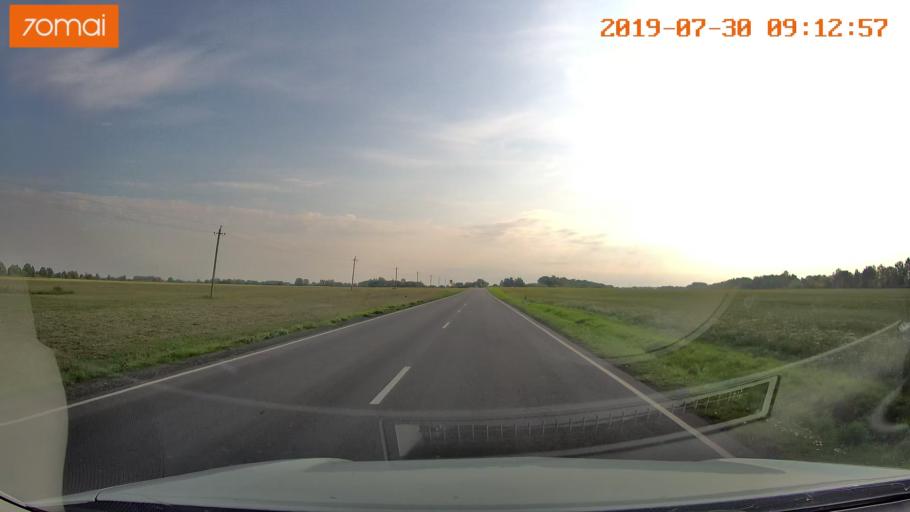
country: RU
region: Kaliningrad
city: Nesterov
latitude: 54.6209
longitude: 22.4868
